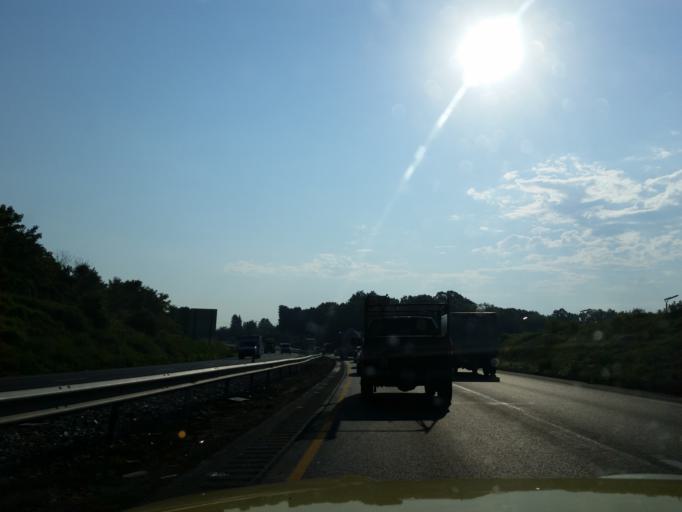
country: US
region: Pennsylvania
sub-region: Lancaster County
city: East Petersburg
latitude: 40.0527
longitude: -76.3760
